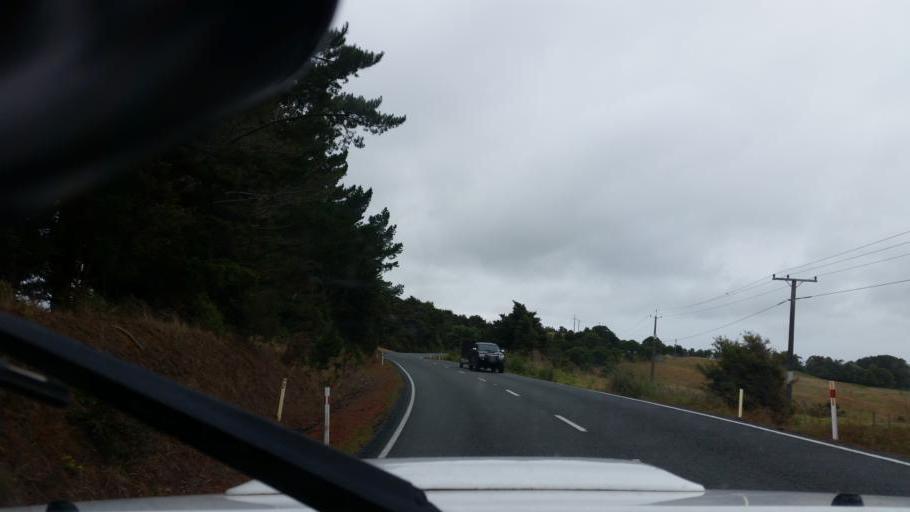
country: NZ
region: Auckland
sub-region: Auckland
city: Wellsford
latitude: -36.1318
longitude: 174.5462
